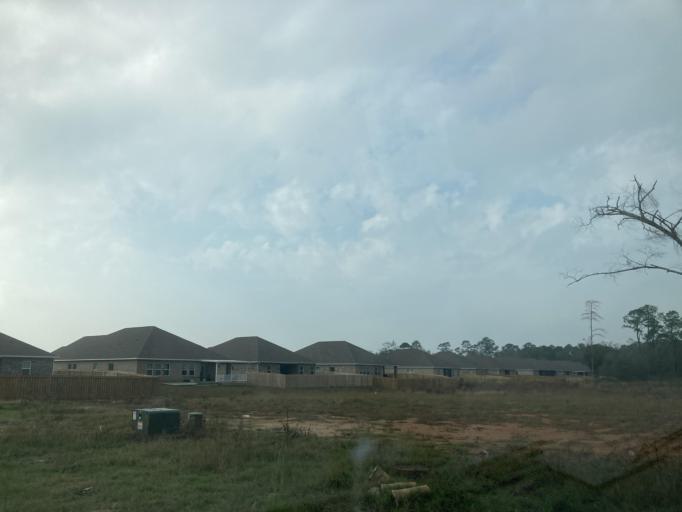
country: US
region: Mississippi
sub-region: Harrison County
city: Long Beach
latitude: 30.3768
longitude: -89.1583
